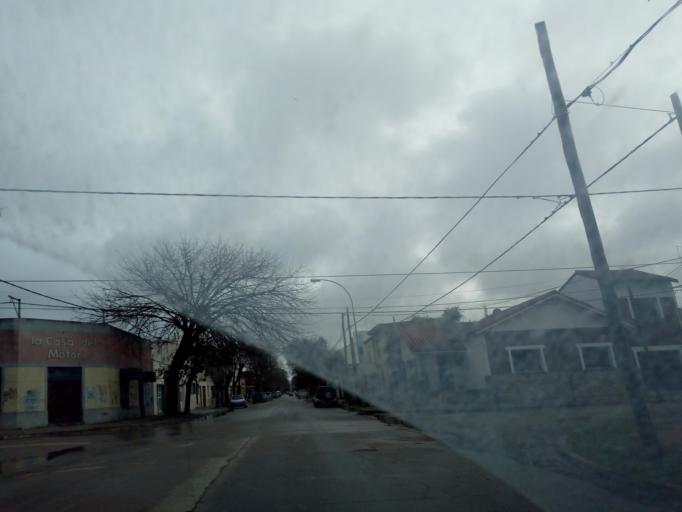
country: AR
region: Buenos Aires
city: Necochea
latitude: -38.5602
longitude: -58.7360
